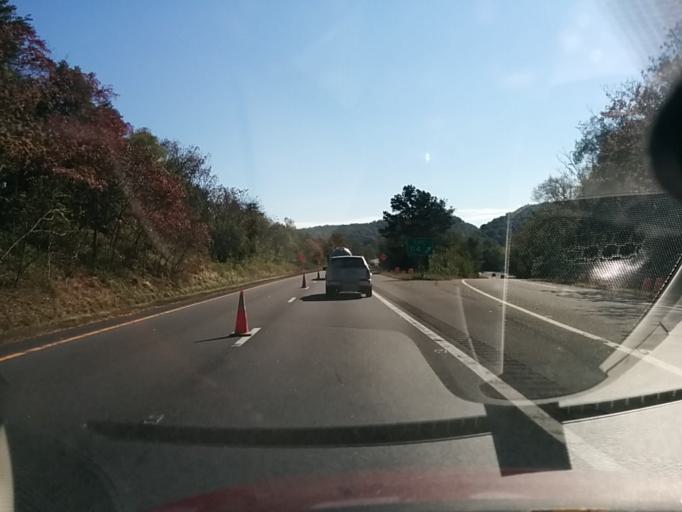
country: US
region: Virginia
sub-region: Albemarle County
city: Crozet
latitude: 38.0348
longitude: -78.6065
